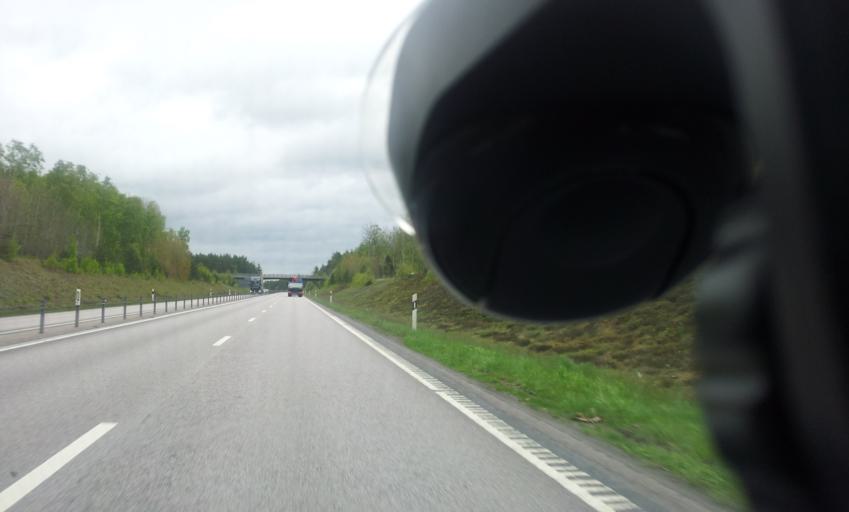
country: SE
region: Kalmar
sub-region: Kalmar Kommun
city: Ljungbyholm
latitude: 56.6272
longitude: 16.1879
